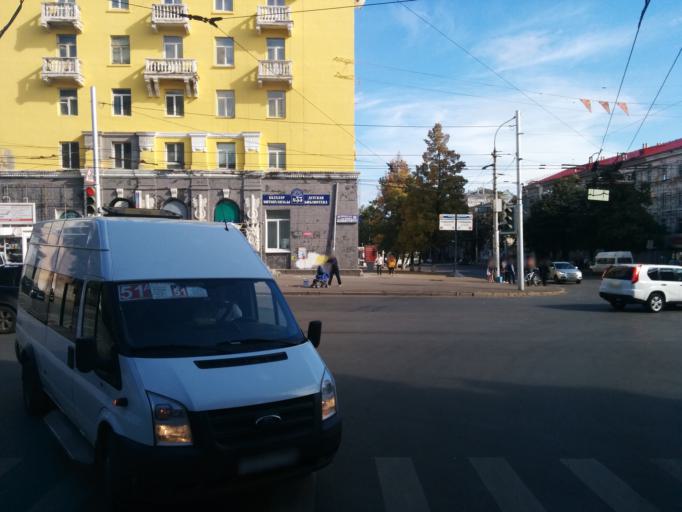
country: RU
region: Bashkortostan
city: Ufa
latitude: 54.8178
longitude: 56.0749
